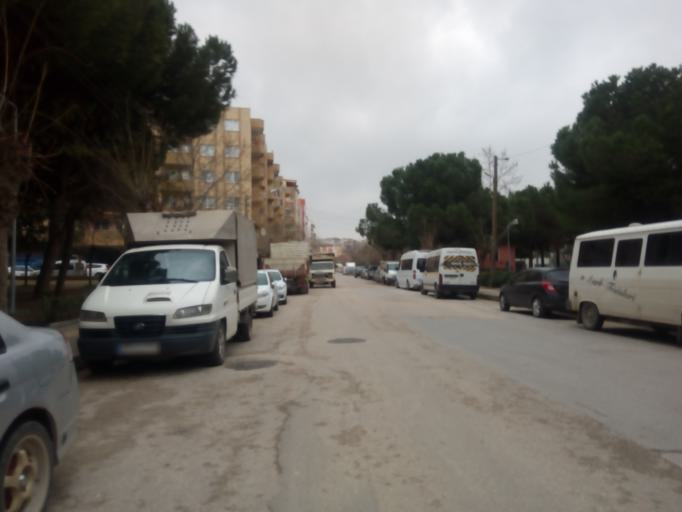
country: TR
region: Bursa
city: Niluefer
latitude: 40.2526
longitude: 28.9613
